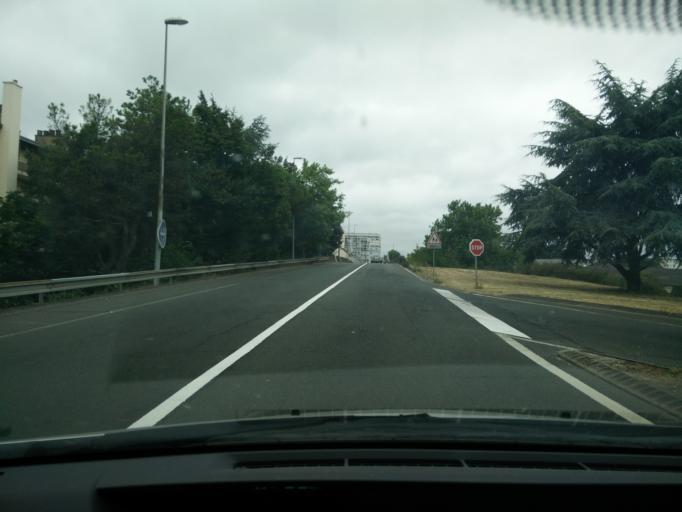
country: FR
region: Pays de la Loire
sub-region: Departement de Maine-et-Loire
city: Angers
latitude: 47.4674
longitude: -0.5280
